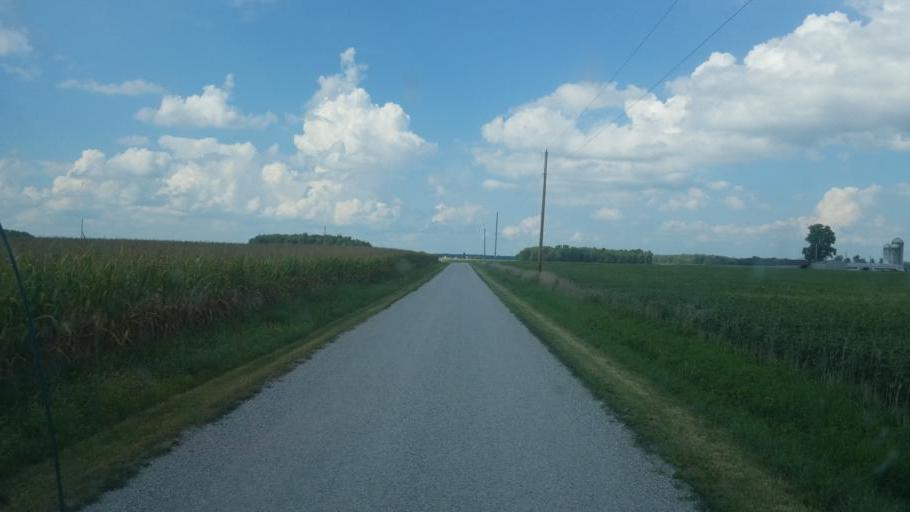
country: US
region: Ohio
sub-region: Huron County
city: Willard
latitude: 40.9942
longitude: -82.7965
